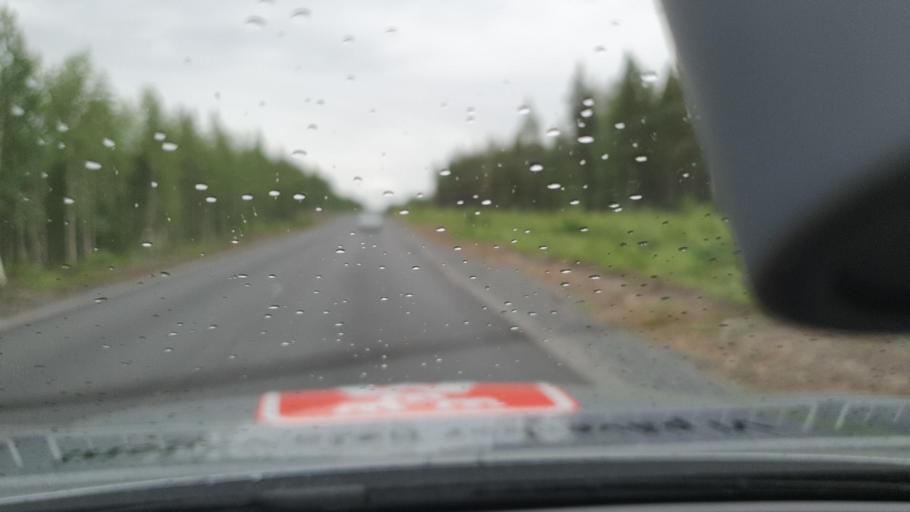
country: SE
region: Norrbotten
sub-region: Overkalix Kommun
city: OEverkalix
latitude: 66.6889
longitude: 23.2095
